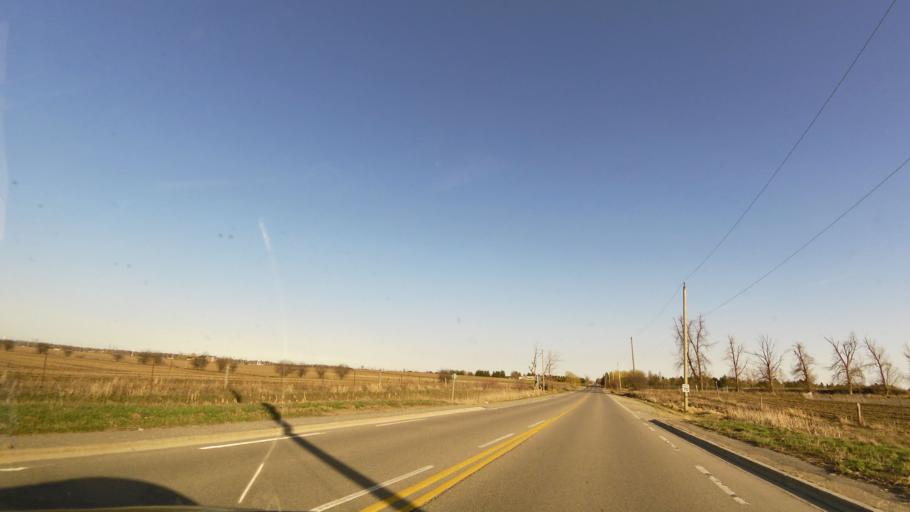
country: CA
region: Ontario
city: Brampton
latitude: 43.8376
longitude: -79.7042
